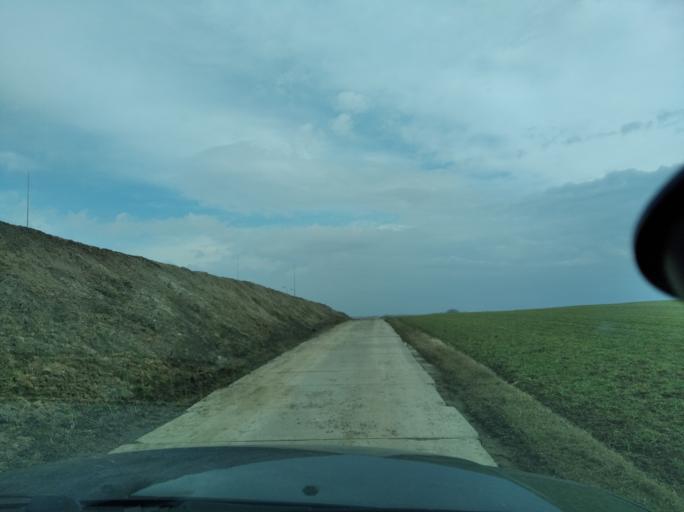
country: PL
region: Subcarpathian Voivodeship
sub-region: Powiat jaroslawski
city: Rokietnica
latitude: 49.9244
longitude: 22.5945
